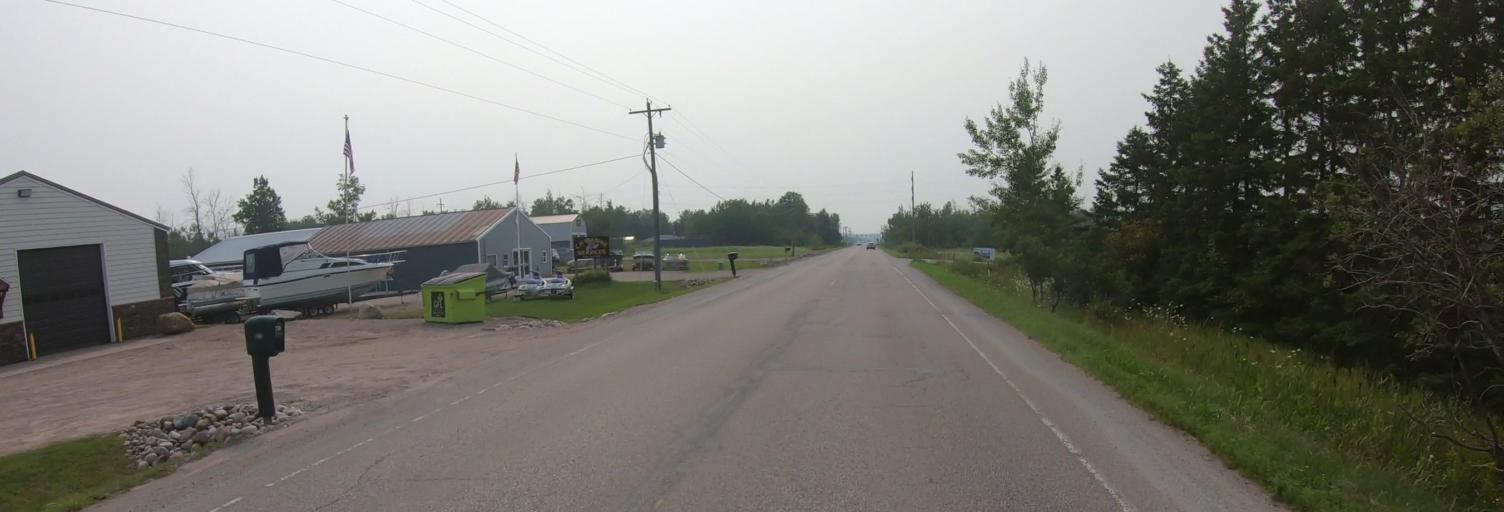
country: US
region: Michigan
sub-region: Chippewa County
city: Sault Ste. Marie
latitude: 46.4632
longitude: -84.3462
